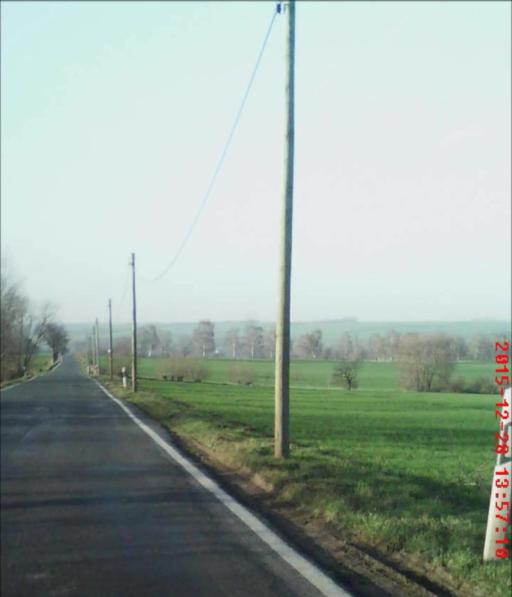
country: DE
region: Thuringia
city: Bad Sulza
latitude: 51.0635
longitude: 11.6166
